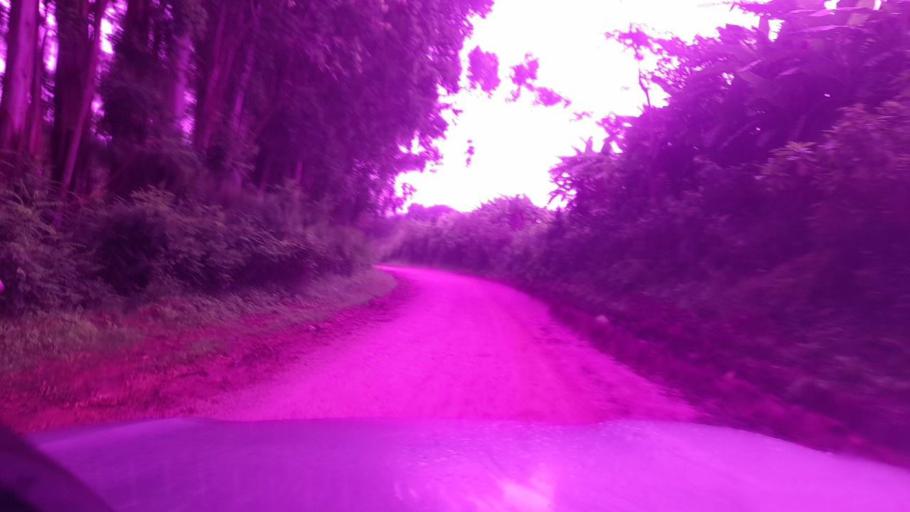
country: ET
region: Southern Nations, Nationalities, and People's Region
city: Bonga
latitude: 7.4615
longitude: 36.1273
